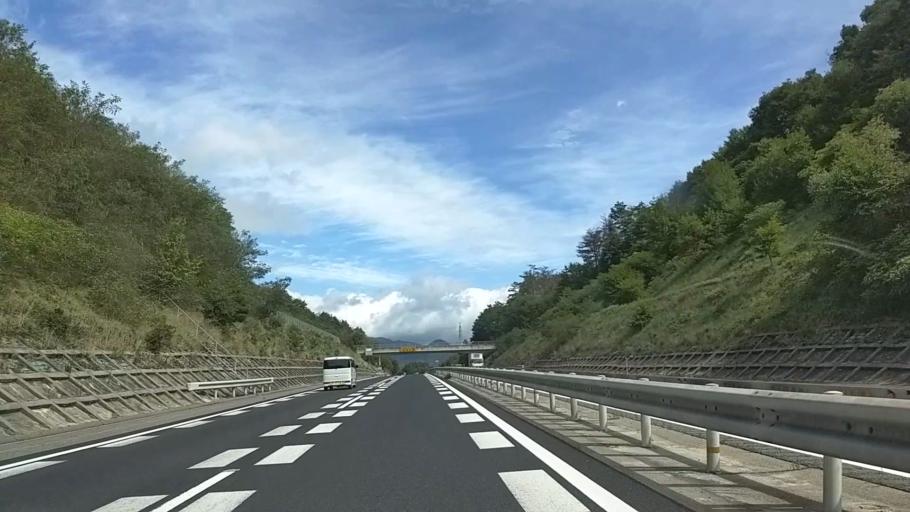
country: JP
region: Nagano
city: Hotaka
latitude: 36.4160
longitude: 138.0038
